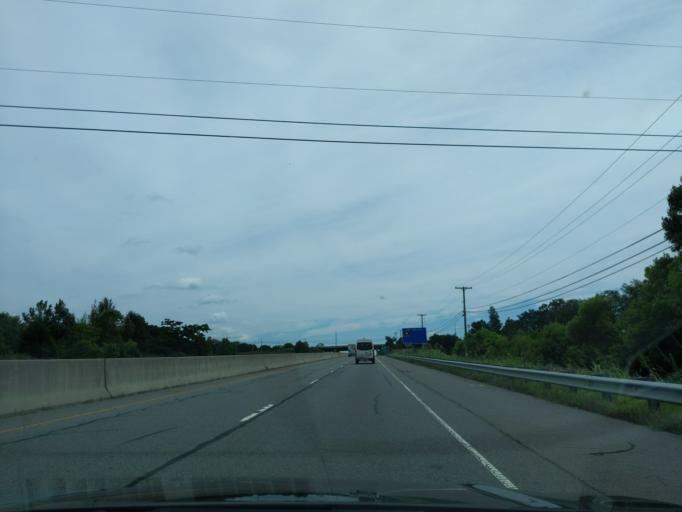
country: US
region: North Carolina
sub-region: Cabarrus County
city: Concord
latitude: 35.3724
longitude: -80.5554
